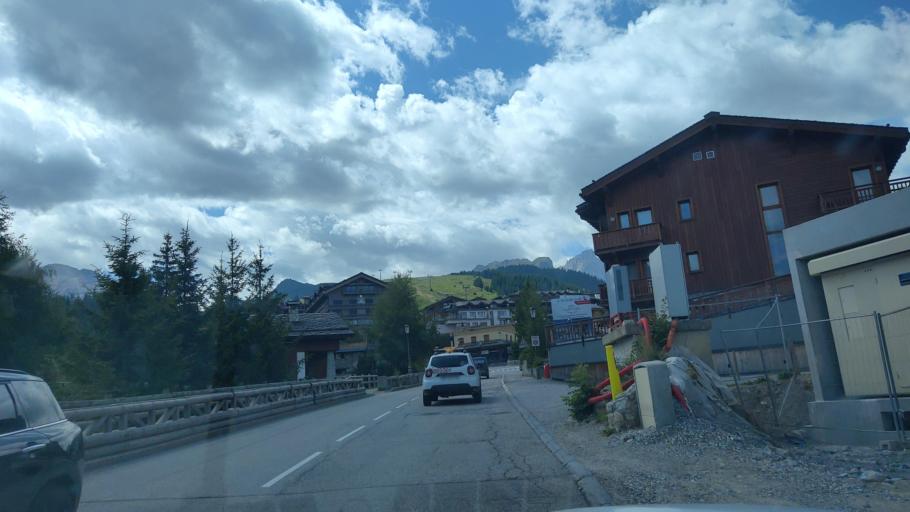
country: FR
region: Rhone-Alpes
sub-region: Departement de la Savoie
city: Courchevel
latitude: 45.4199
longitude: 6.6531
